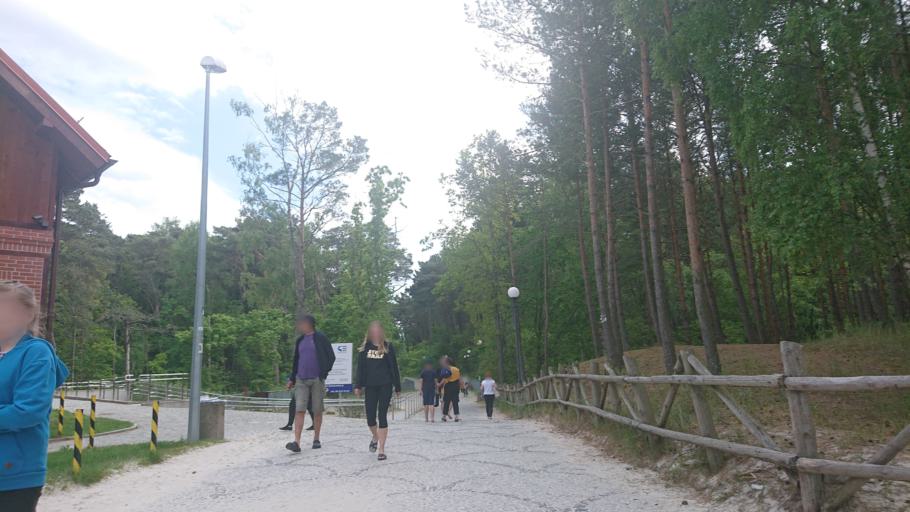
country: PL
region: Pomeranian Voivodeship
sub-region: Powiat pucki
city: Krokowa
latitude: 54.8325
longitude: 18.0881
